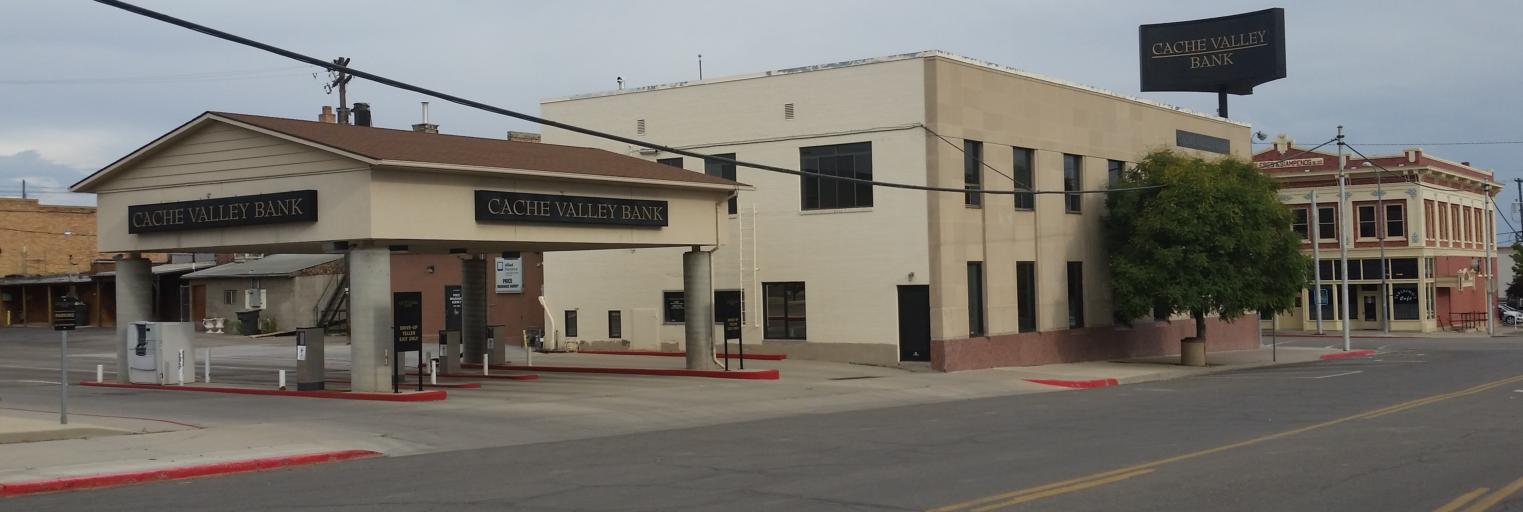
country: US
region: Utah
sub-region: Carbon County
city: Price
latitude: 39.6009
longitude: -110.8135
